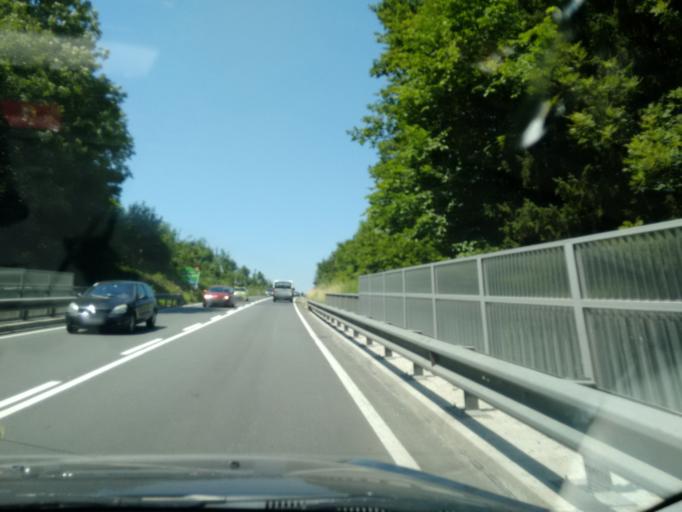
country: AT
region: Upper Austria
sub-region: Politischer Bezirk Gmunden
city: Altmunster
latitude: 47.9525
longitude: 13.7464
